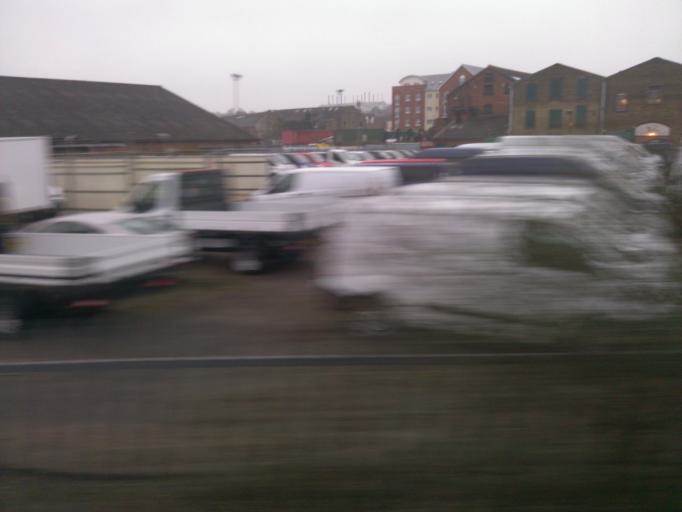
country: GB
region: England
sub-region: Essex
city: Colchester
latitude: 51.8849
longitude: 0.9287
